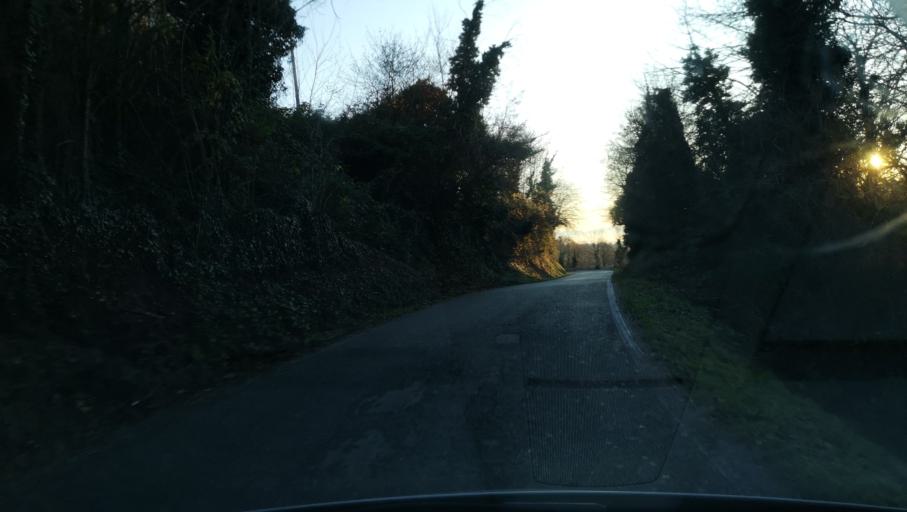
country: IT
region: Piedmont
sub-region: Provincia di Asti
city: Moncucco Torinese
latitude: 45.0777
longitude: 7.9296
